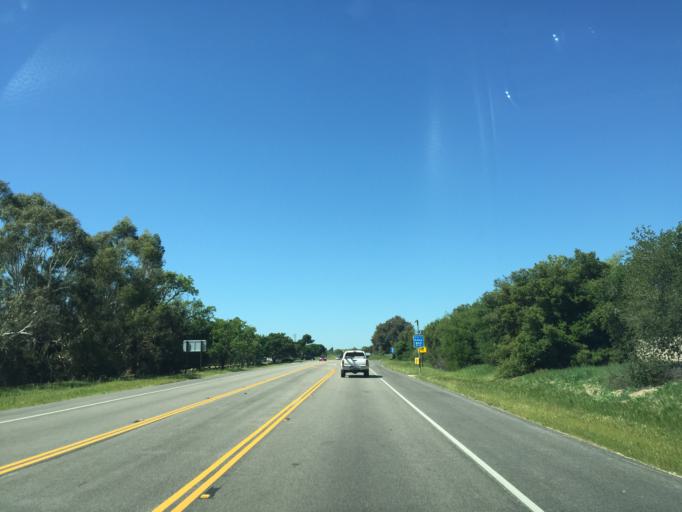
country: US
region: California
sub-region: Santa Barbara County
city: Los Olivos
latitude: 34.6565
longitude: -120.1003
